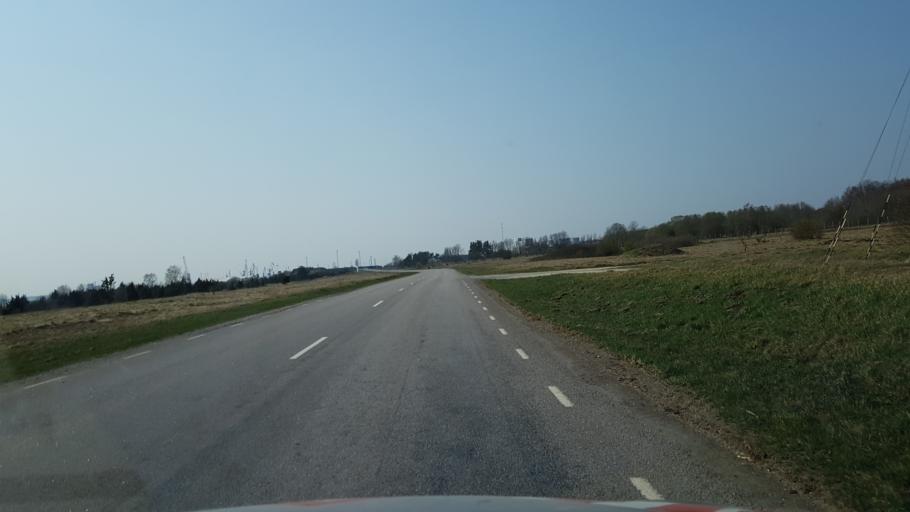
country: EE
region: Harju
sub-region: Paldiski linn
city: Paldiski
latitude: 59.3294
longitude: 24.1082
